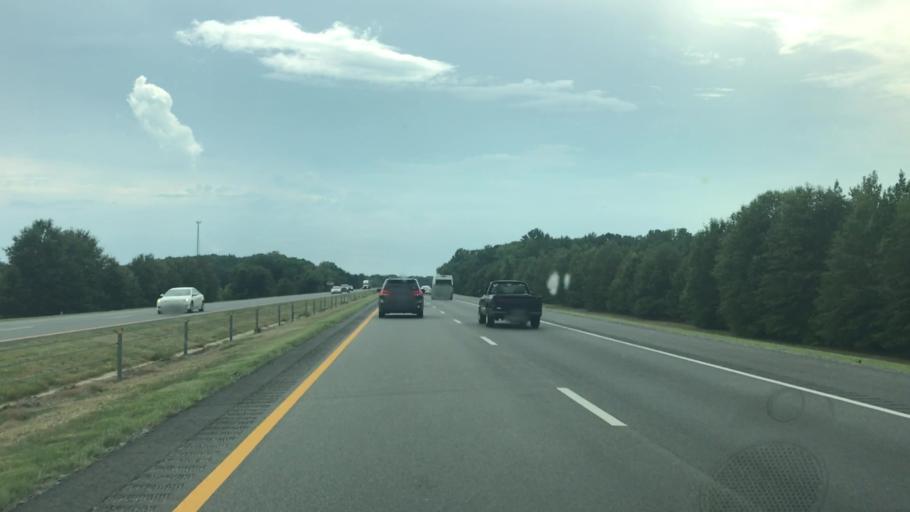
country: US
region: Arkansas
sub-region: Monroe County
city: Brinkley
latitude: 34.8805
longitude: -91.2658
